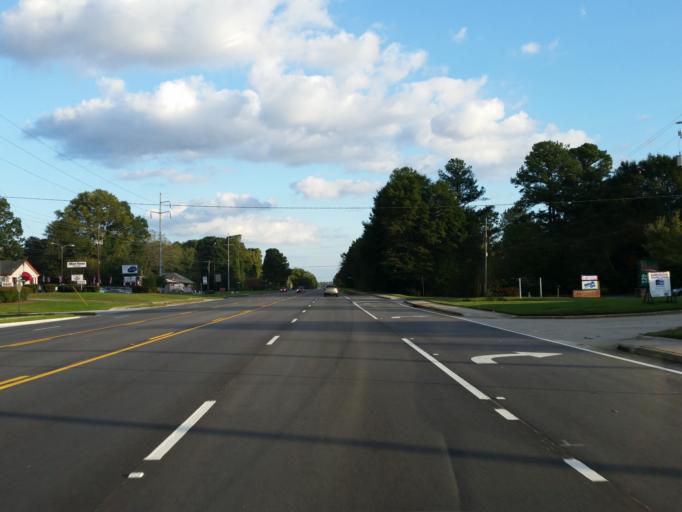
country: US
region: Georgia
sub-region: Cobb County
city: Smyrna
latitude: 33.8702
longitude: -84.5275
